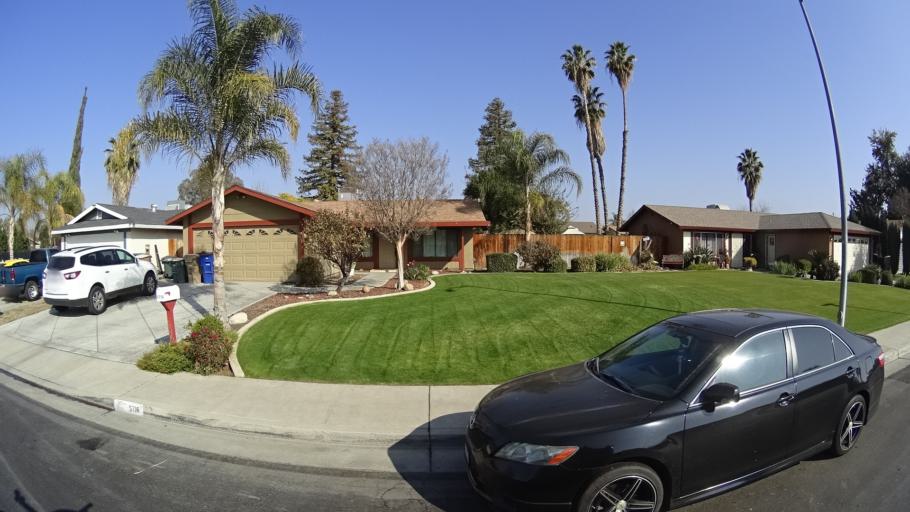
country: US
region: California
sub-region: Kern County
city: Bakersfield
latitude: 35.3199
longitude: -119.0674
